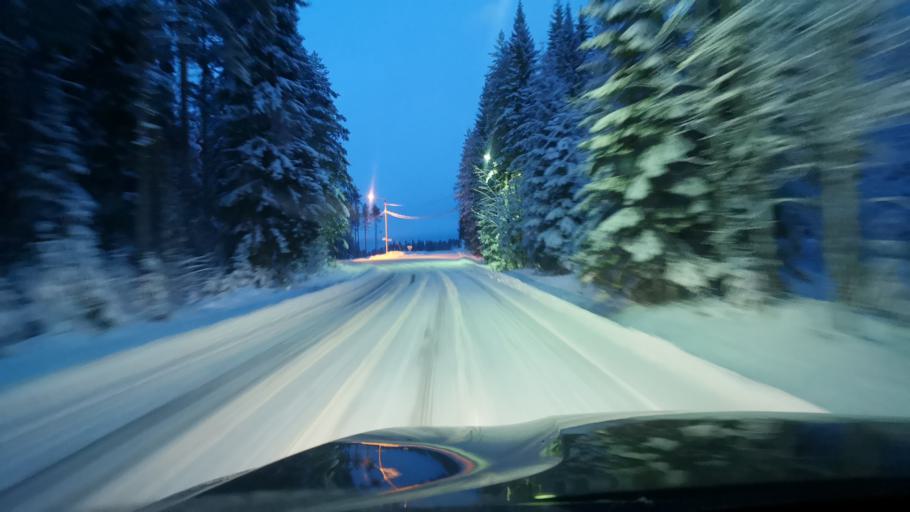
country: FI
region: Varsinais-Suomi
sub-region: Loimaa
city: Loimaa
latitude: 60.8696
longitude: 23.0892
